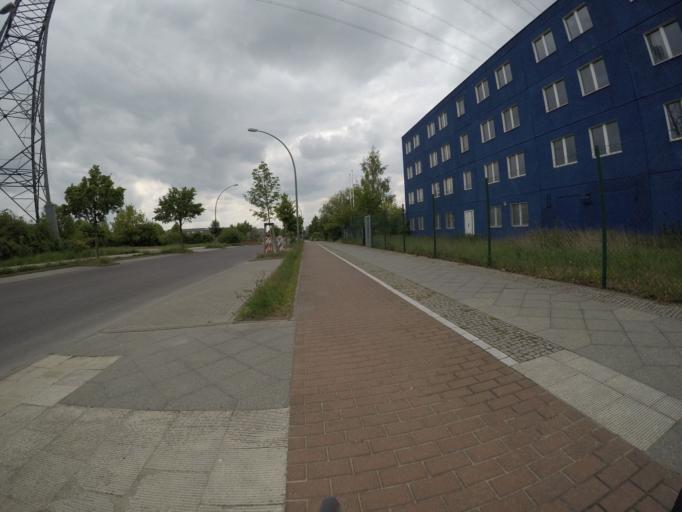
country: DE
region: Berlin
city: Falkenberg
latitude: 52.5506
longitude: 13.5373
